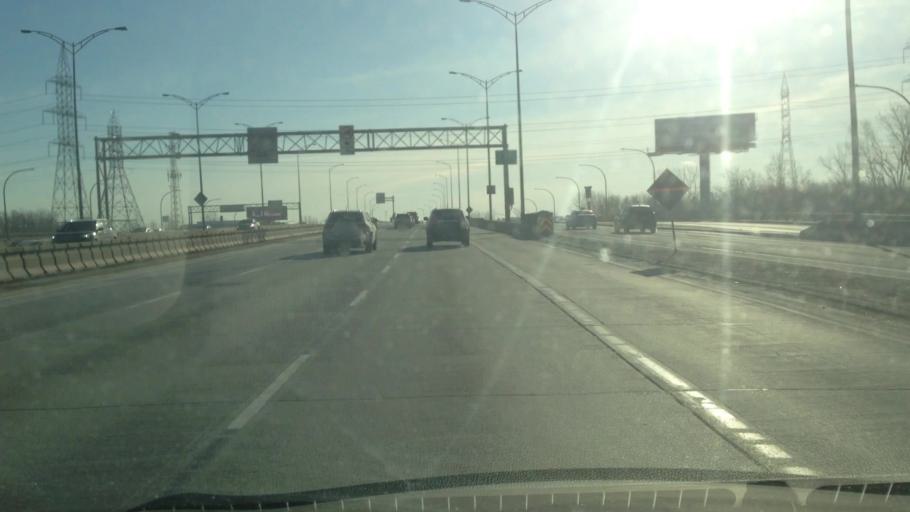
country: CA
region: Quebec
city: Dorval
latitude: 45.5064
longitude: -73.7596
